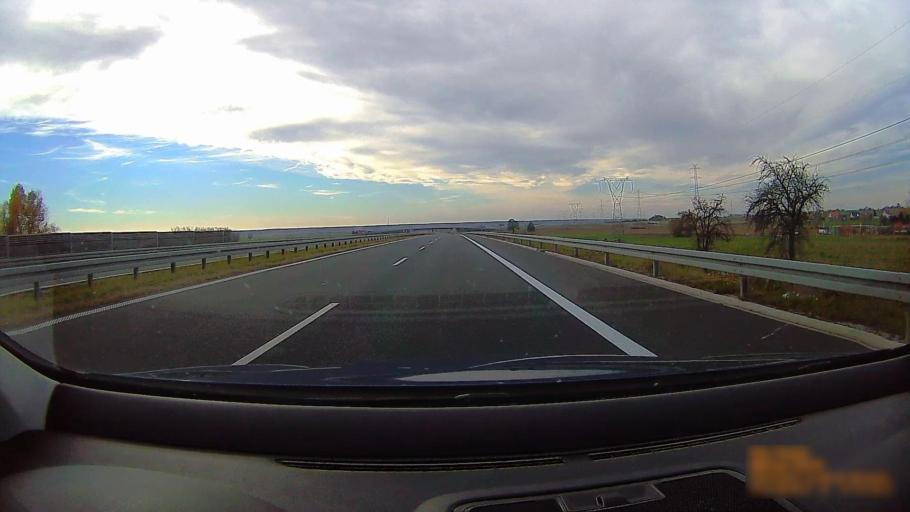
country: PL
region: Greater Poland Voivodeship
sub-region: Powiat ostrowski
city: Przygodzice
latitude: 51.6049
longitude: 17.8538
